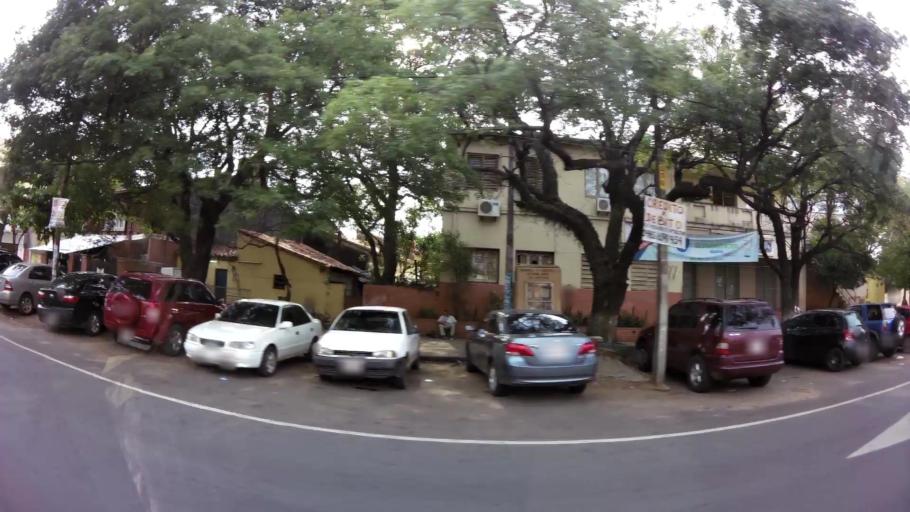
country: PY
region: Asuncion
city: Asuncion
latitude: -25.2999
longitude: -57.6130
